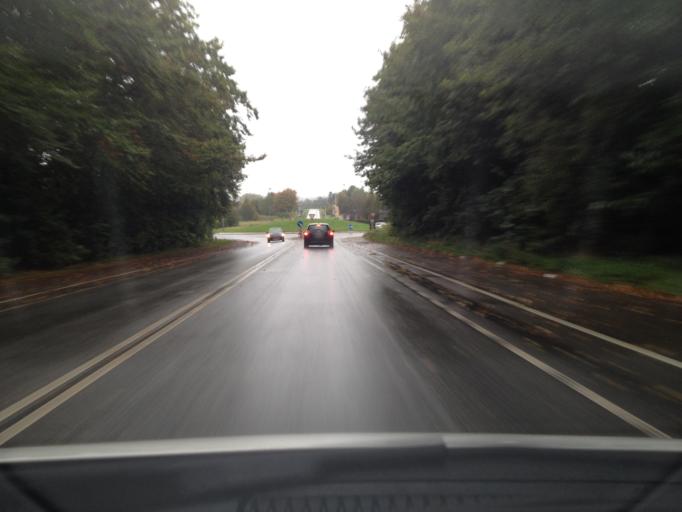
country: DK
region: Zealand
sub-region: Holbaek Kommune
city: Tollose
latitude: 55.5425
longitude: 11.7092
